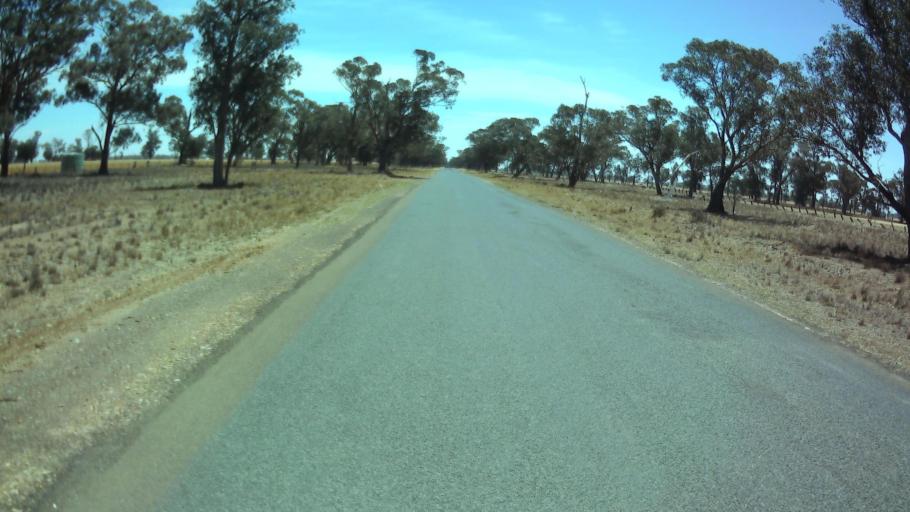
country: AU
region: New South Wales
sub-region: Weddin
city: Grenfell
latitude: -34.0071
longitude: 147.7791
